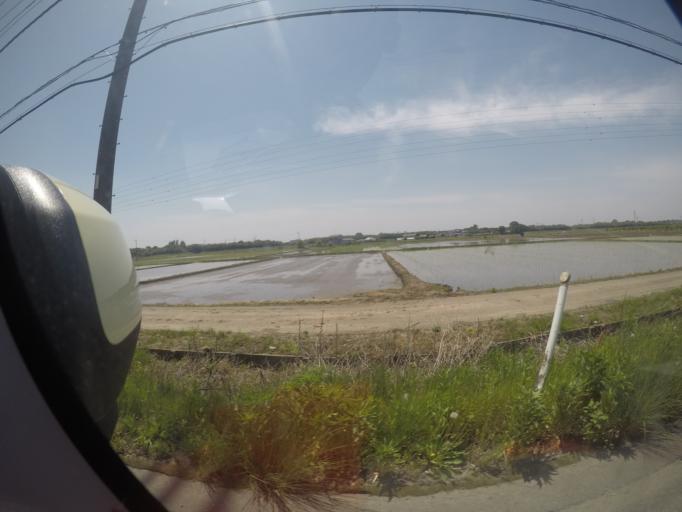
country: JP
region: Ibaraki
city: Tsukuba
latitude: 36.2148
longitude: 140.0681
